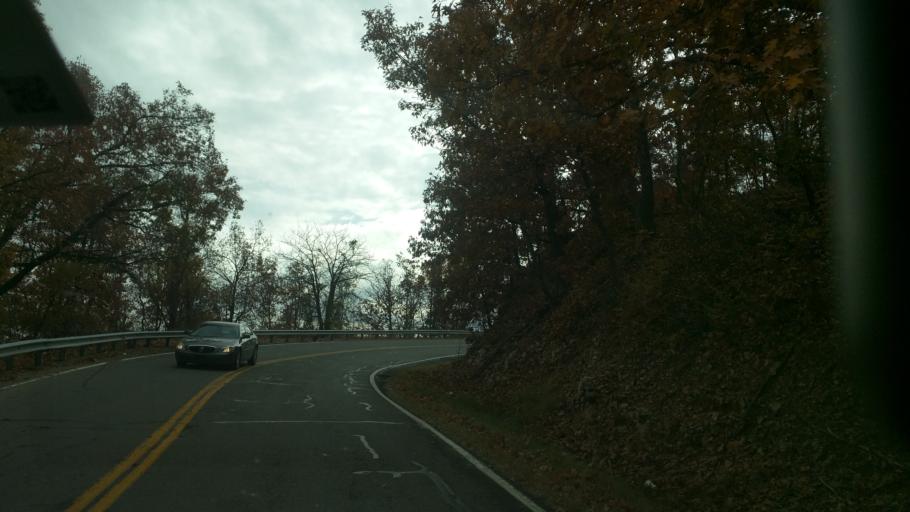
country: US
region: Oklahoma
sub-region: Cherokee County
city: Tahlequah
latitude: 35.9245
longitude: -94.8441
